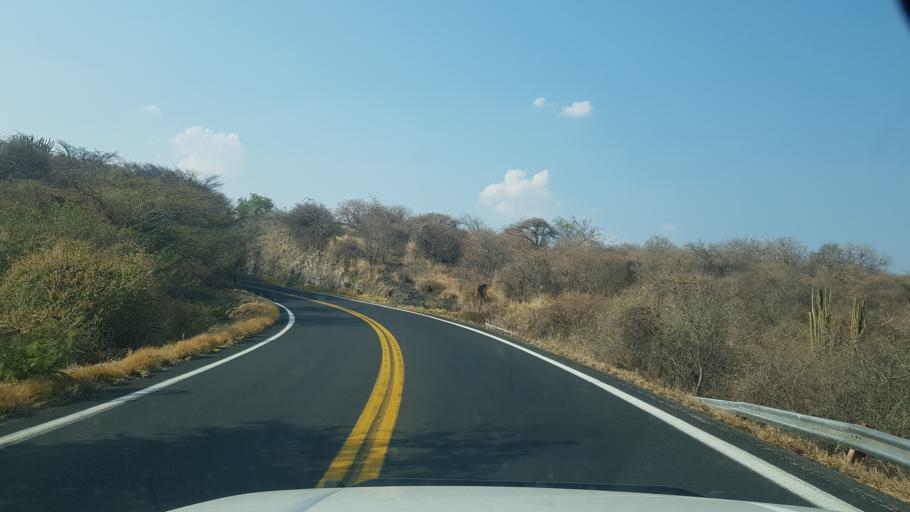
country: MX
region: Puebla
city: Calmeca
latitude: 18.6513
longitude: -98.6641
